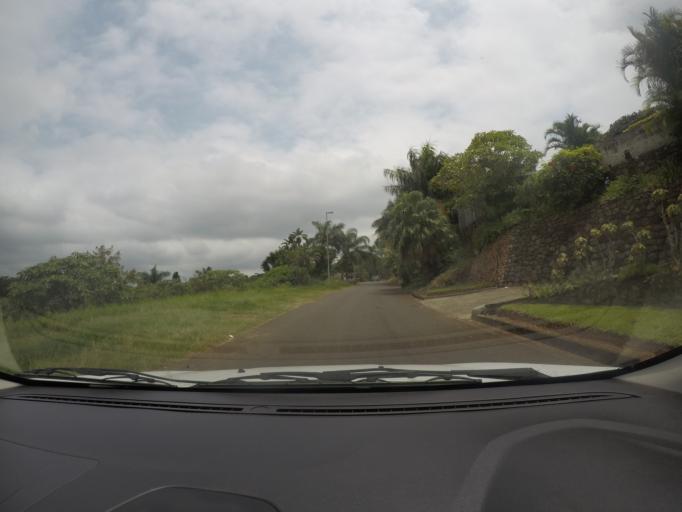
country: ZA
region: KwaZulu-Natal
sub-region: uThungulu District Municipality
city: Empangeni
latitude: -28.7510
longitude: 31.8881
